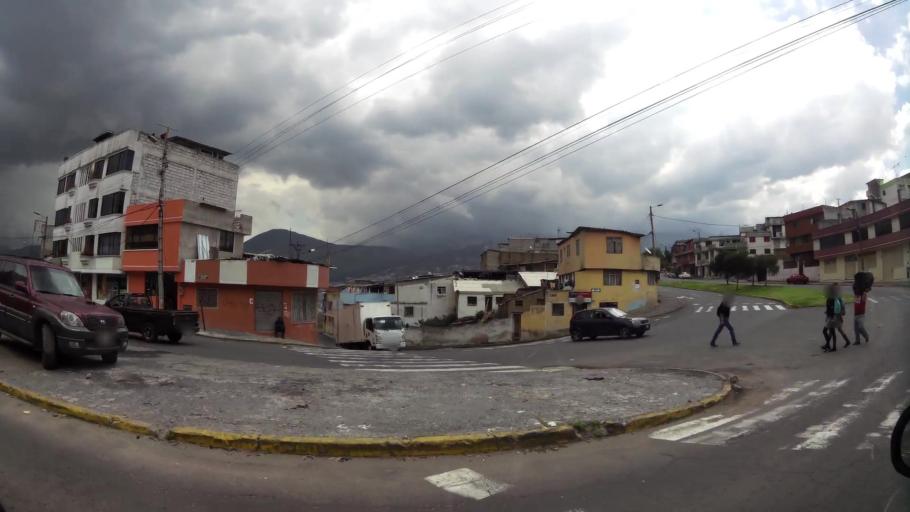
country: EC
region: Pichincha
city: Quito
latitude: -0.2509
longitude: -78.5124
